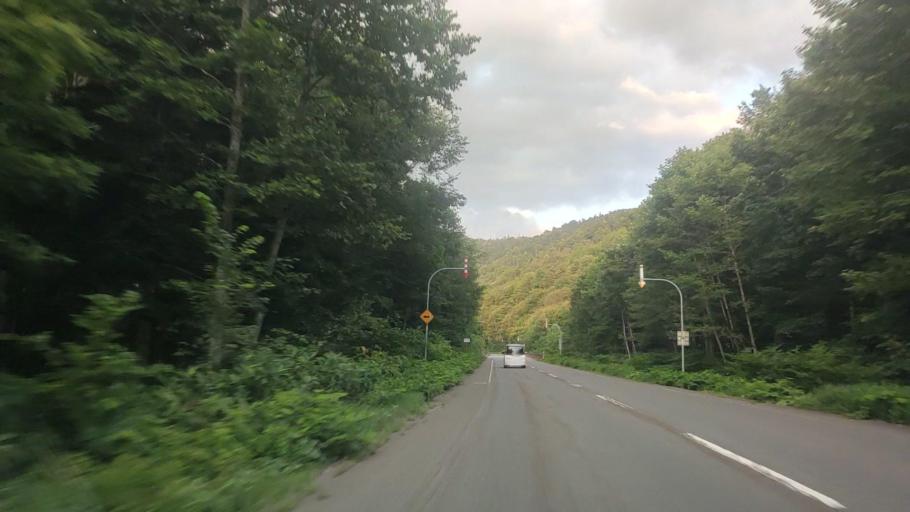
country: JP
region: Hokkaido
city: Ashibetsu
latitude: 43.3750
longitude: 142.1998
